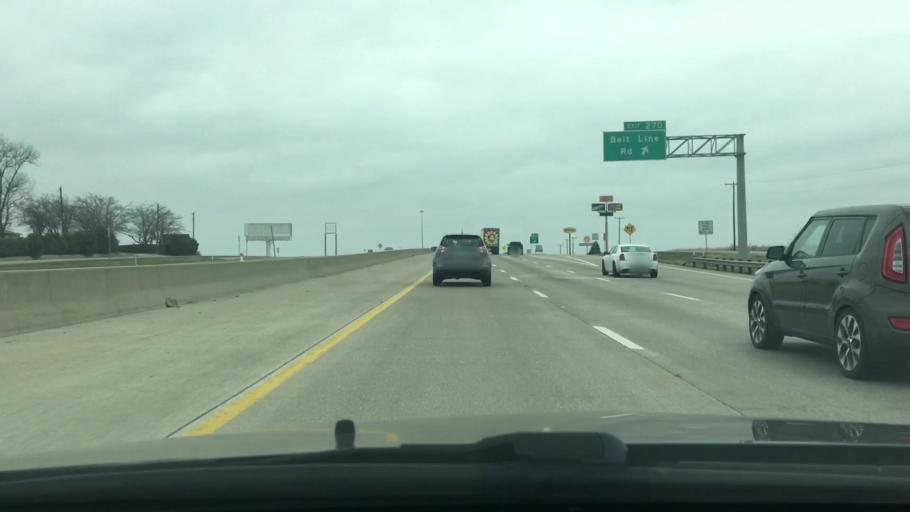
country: US
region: Texas
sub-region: Dallas County
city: Wilmer
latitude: 32.5958
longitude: -96.6817
